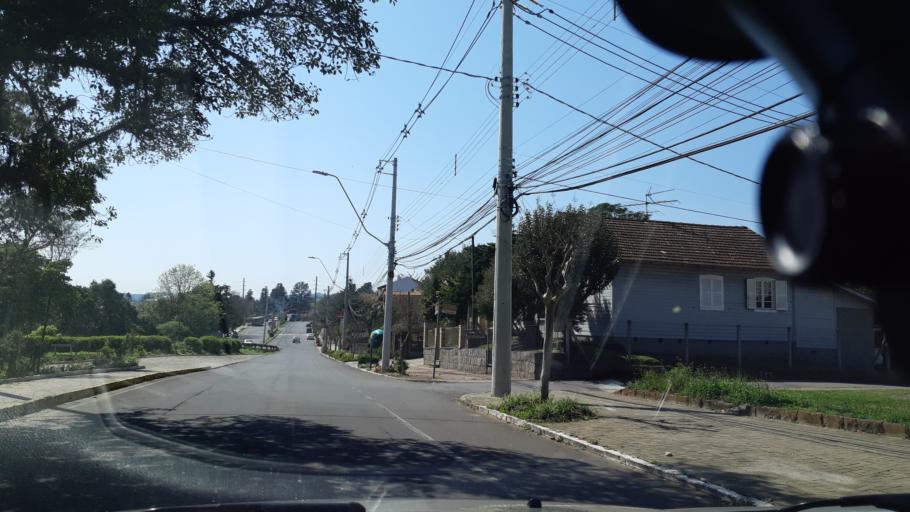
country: BR
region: Rio Grande do Sul
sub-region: Nova Petropolis
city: Nova Petropolis
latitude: -29.3839
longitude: -51.1196
